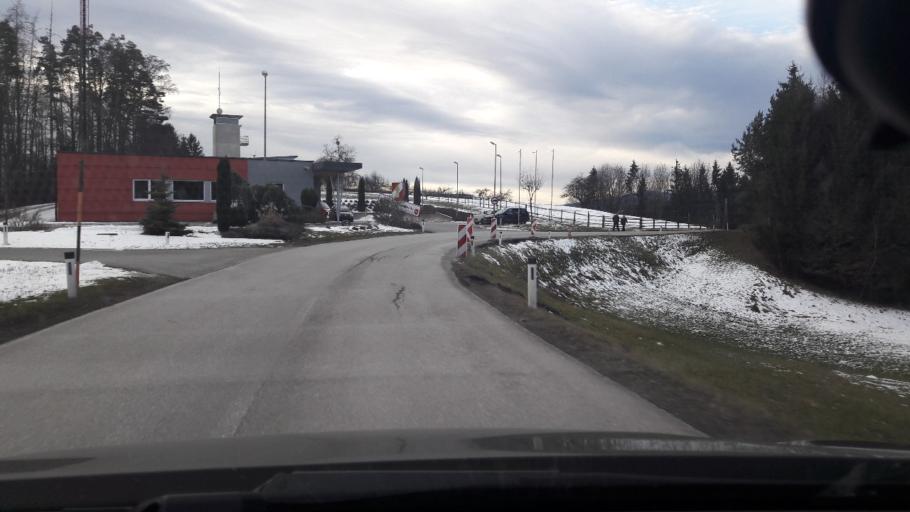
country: AT
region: Styria
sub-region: Politischer Bezirk Graz-Umgebung
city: Sankt Oswald bei Plankenwarth
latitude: 47.0848
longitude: 15.2766
